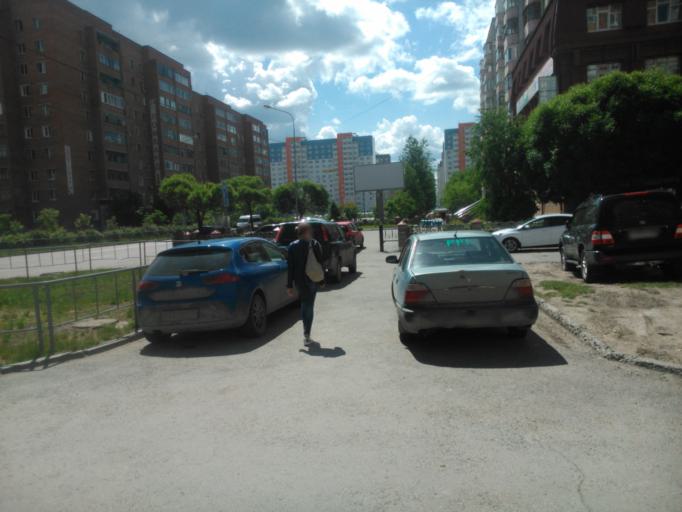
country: RU
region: Tjumen
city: Tyumen
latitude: 57.1051
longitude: 65.6035
